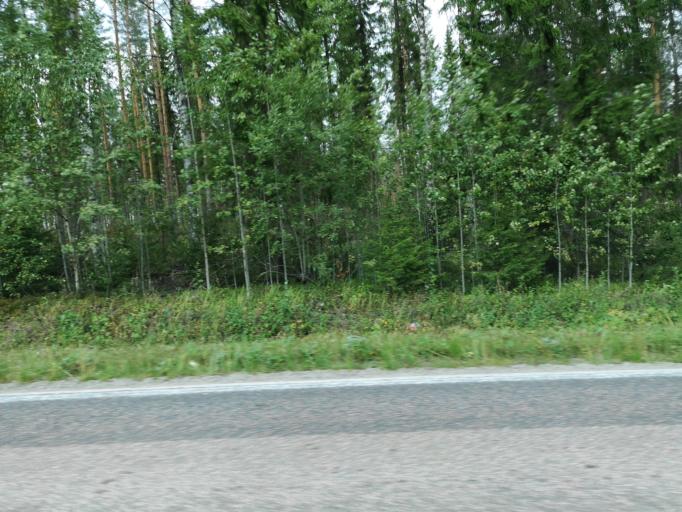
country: FI
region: Central Finland
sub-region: Jyvaeskylae
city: Hankasalmi
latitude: 62.3521
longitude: 26.4611
